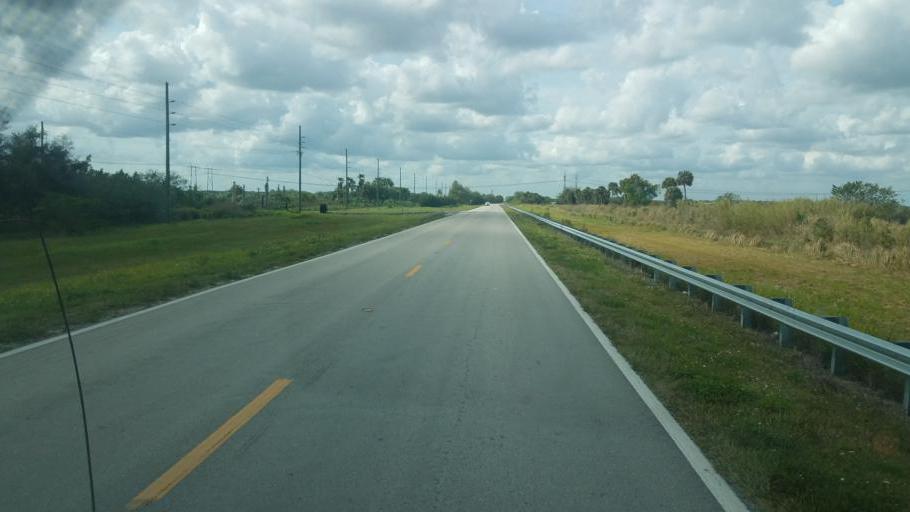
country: US
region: Florida
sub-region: Saint Lucie County
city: Lakewood Park
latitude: 27.4477
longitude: -80.5372
